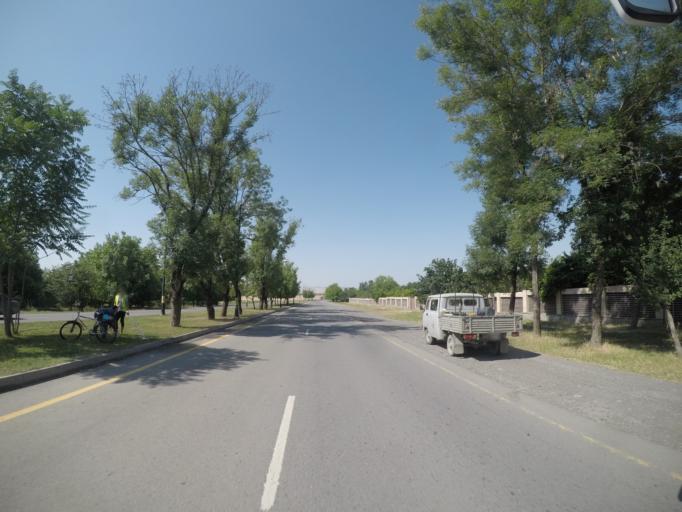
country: AZ
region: Qabala Rayon
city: Qutqashen
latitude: 40.8580
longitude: 47.7538
